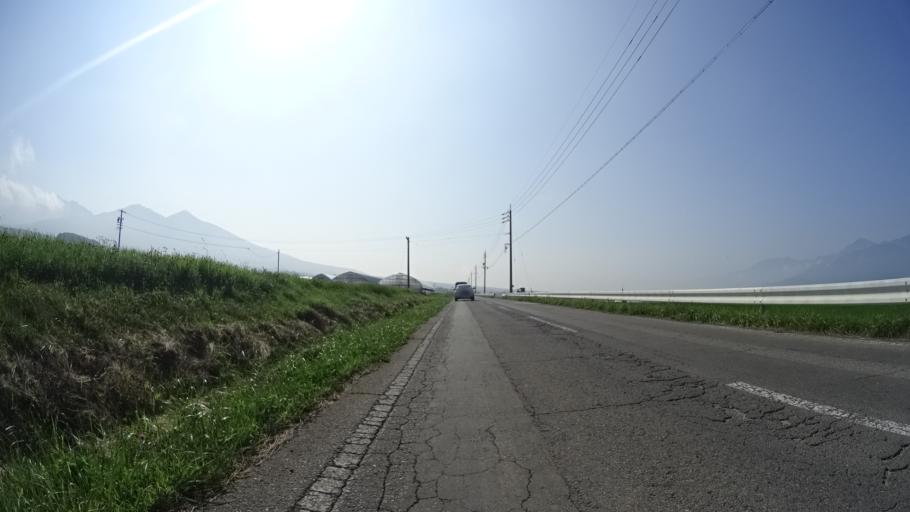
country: JP
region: Nagano
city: Chino
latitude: 35.9427
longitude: 138.2497
